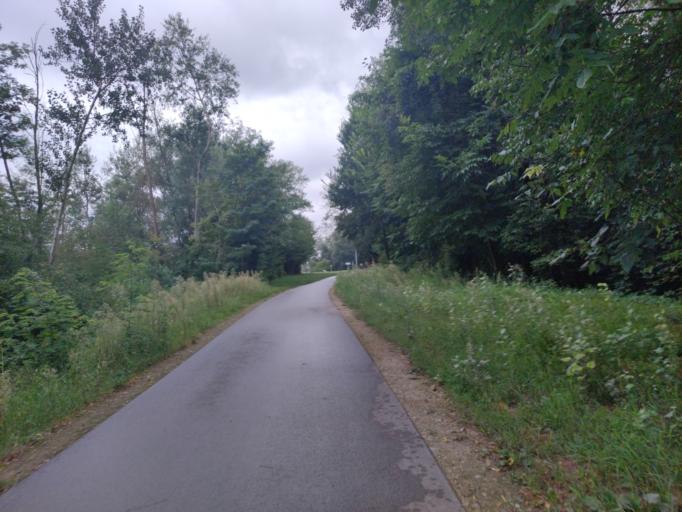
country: AT
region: Lower Austria
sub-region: Politischer Bezirk Korneuburg
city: Spillern
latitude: 48.3496
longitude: 16.2425
